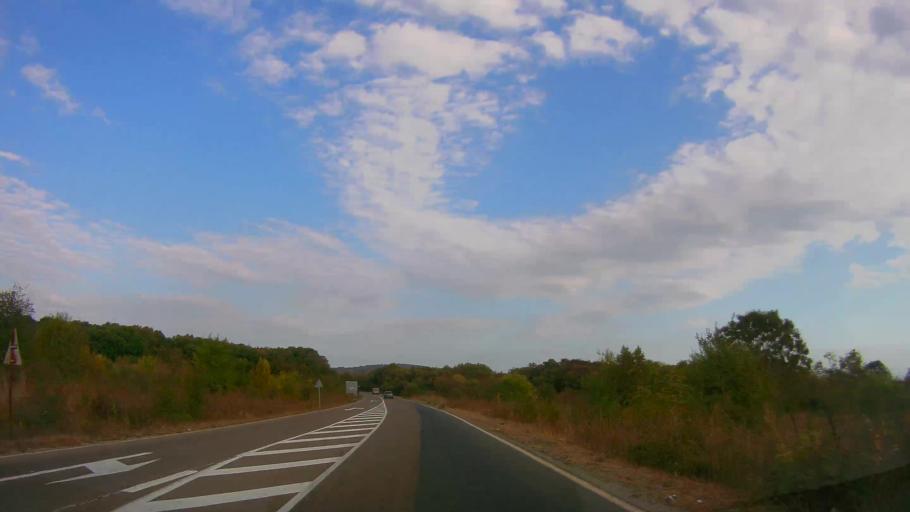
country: BG
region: Burgas
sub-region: Obshtina Sozopol
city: Sozopol
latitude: 42.3467
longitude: 27.7143
